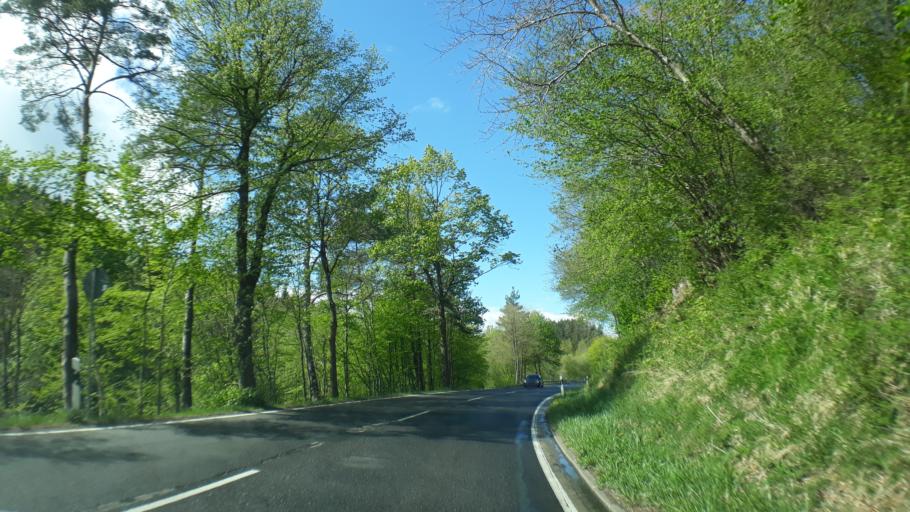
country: DE
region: North Rhine-Westphalia
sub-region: Regierungsbezirk Koln
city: Kall
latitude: 50.5158
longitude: 6.5653
